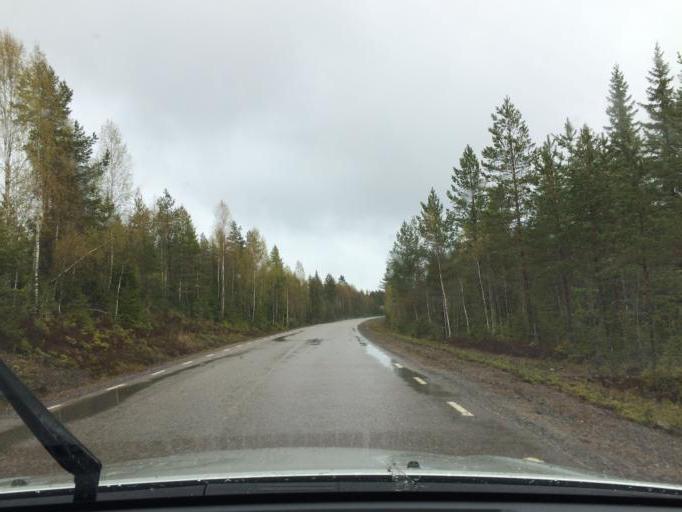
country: SE
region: Dalarna
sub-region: Ludvika Kommun
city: Abborrberget
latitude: 60.0583
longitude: 14.8001
